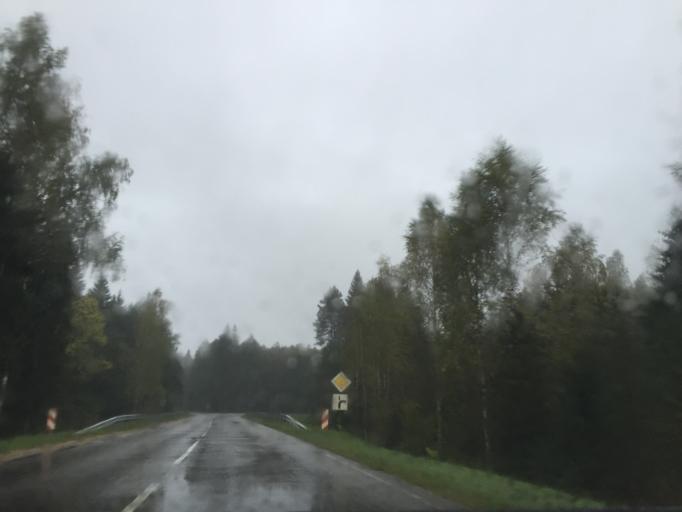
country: LV
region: Ropazu
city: Ropazi
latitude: 57.0120
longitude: 24.6811
